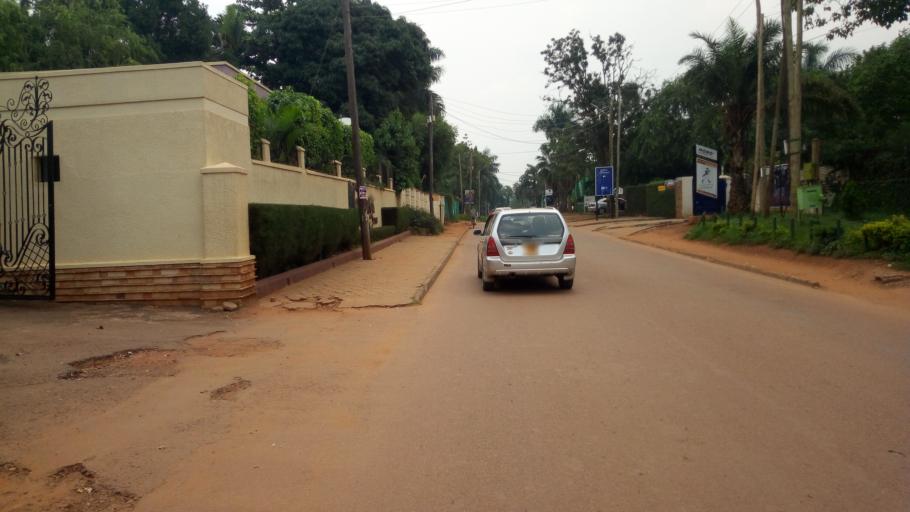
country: UG
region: Central Region
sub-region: Wakiso District
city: Kireka
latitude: 0.3181
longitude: 32.6225
